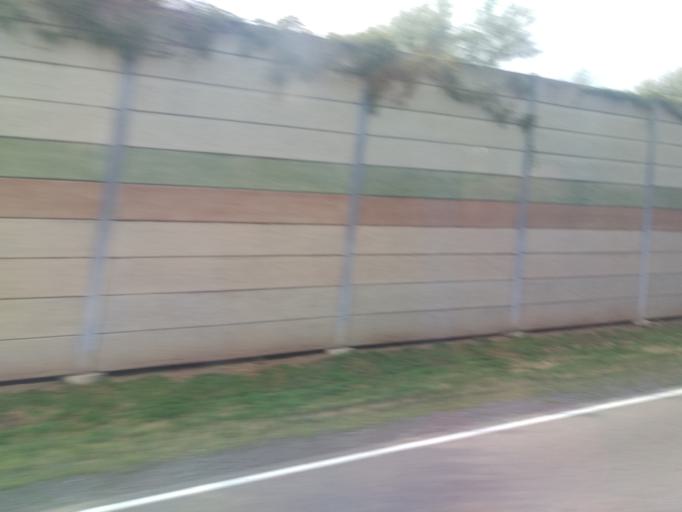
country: CA
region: Ontario
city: Mississauga
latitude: 43.5315
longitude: -79.6393
